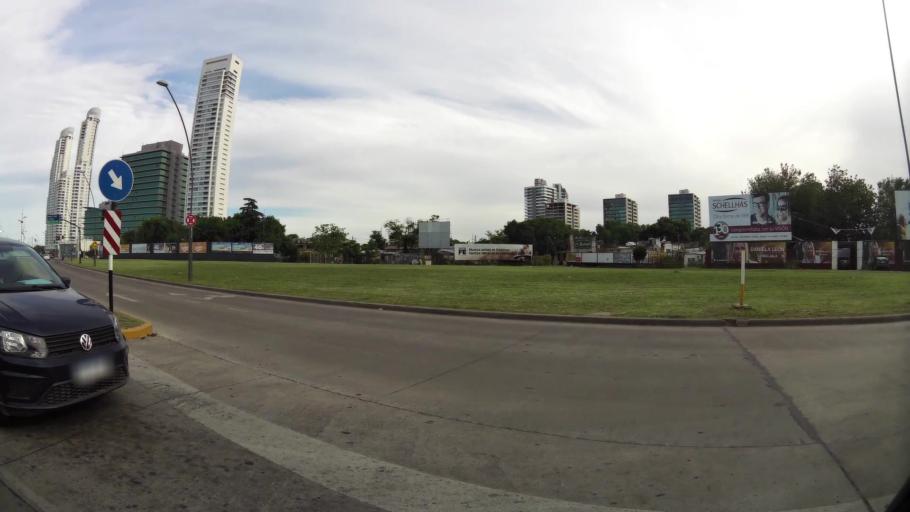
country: AR
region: Santa Fe
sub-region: Departamento de Rosario
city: Rosario
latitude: -32.9247
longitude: -60.6629
